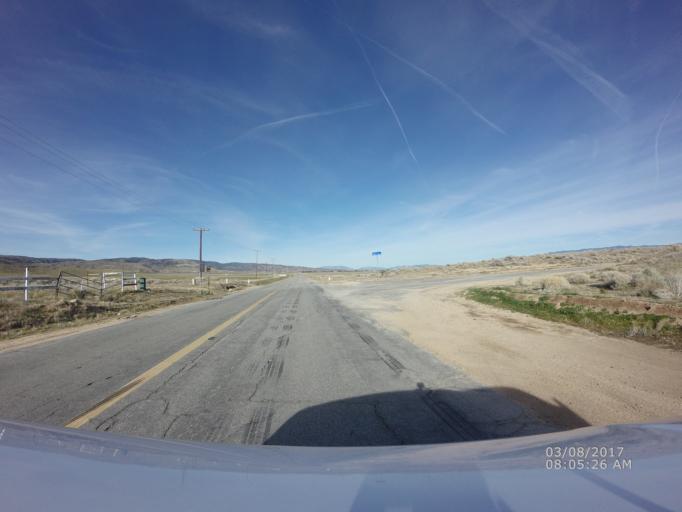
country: US
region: California
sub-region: Los Angeles County
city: Green Valley
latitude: 34.7391
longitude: -118.4309
